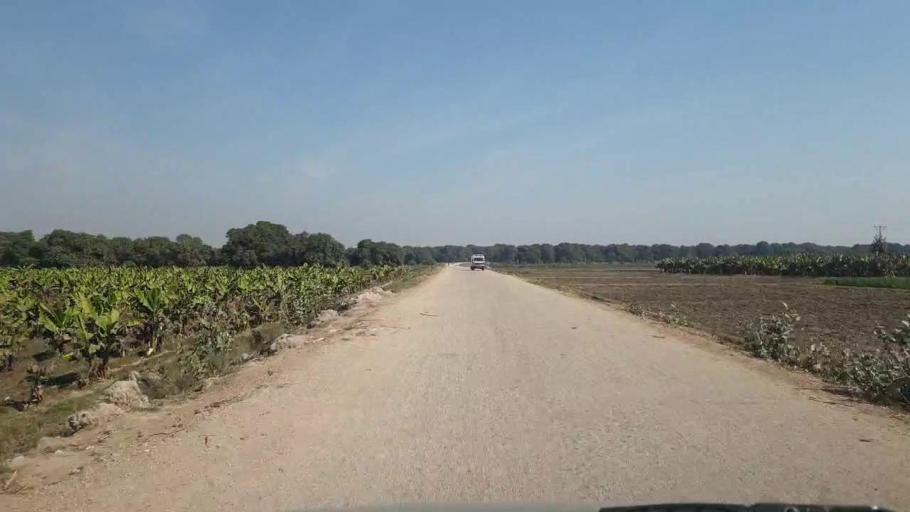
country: PK
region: Sindh
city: Tando Allahyar
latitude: 25.3988
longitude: 68.7719
